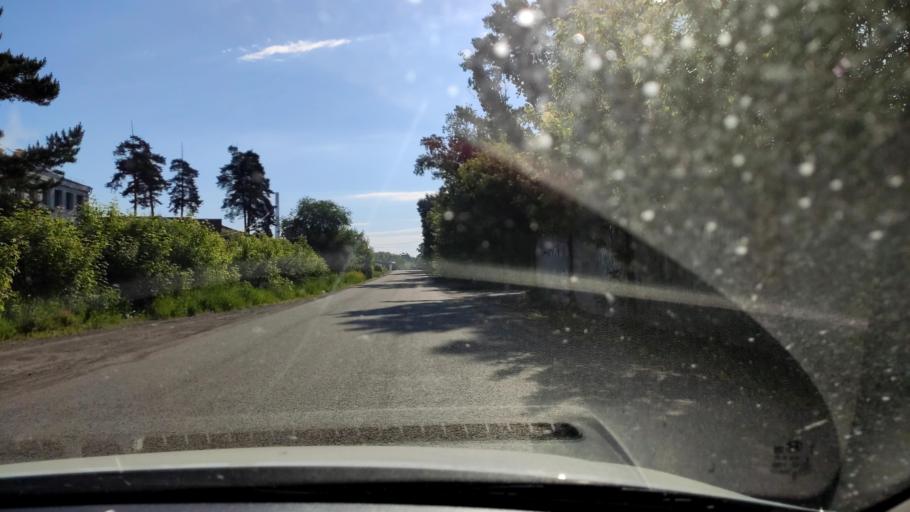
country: RU
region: Tatarstan
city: Staroye Arakchino
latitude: 55.8401
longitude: 49.0395
